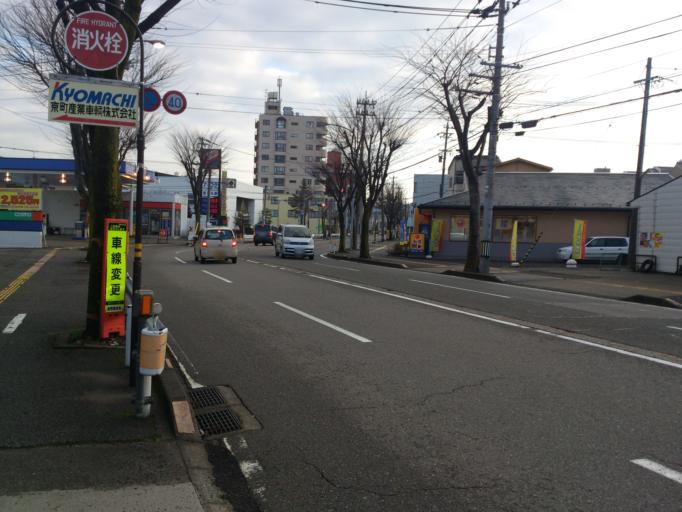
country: JP
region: Ishikawa
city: Kanazawa-shi
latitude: 36.5805
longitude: 136.6562
